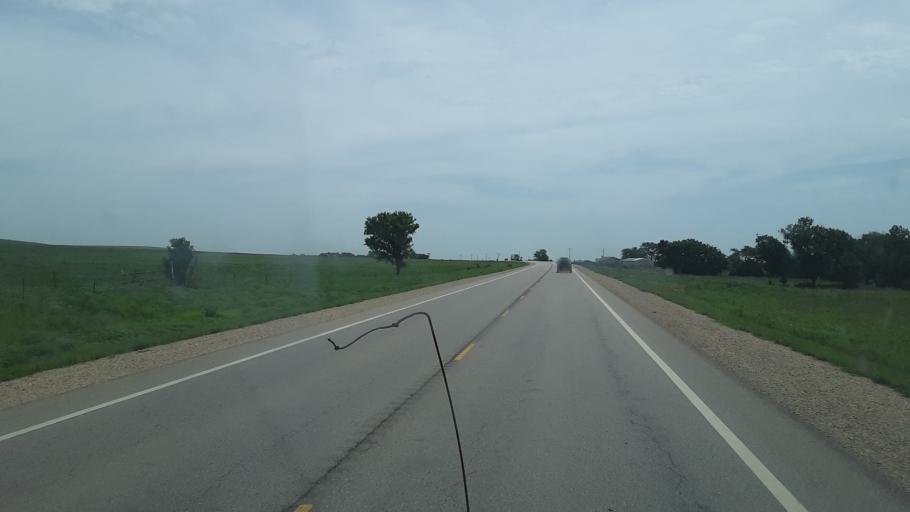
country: US
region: Kansas
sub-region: Greenwood County
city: Eureka
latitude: 37.8116
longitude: -96.4583
